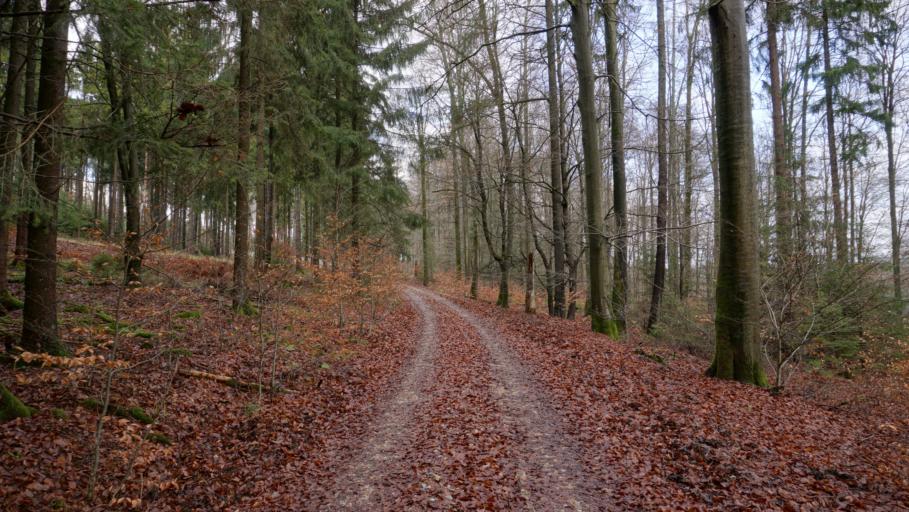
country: DE
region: Baden-Wuerttemberg
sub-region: Karlsruhe Region
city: Fahrenbach
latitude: 49.4317
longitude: 9.1180
